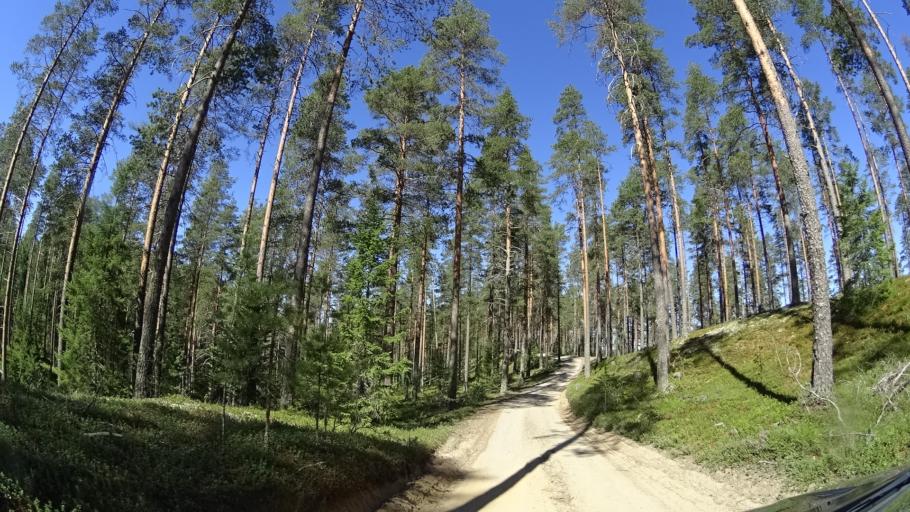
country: FI
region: Kainuu
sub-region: Kajaani
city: Vuolijoki
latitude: 63.9709
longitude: 26.8031
